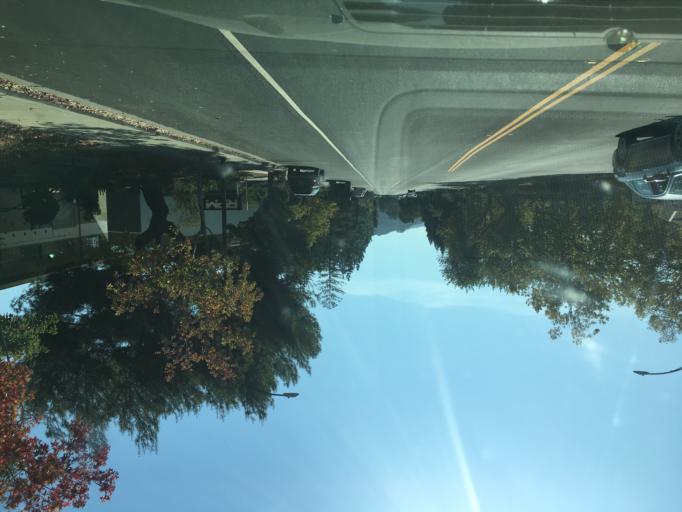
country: US
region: California
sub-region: Santa Clara County
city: Los Gatos
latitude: 37.2406
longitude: -121.9735
